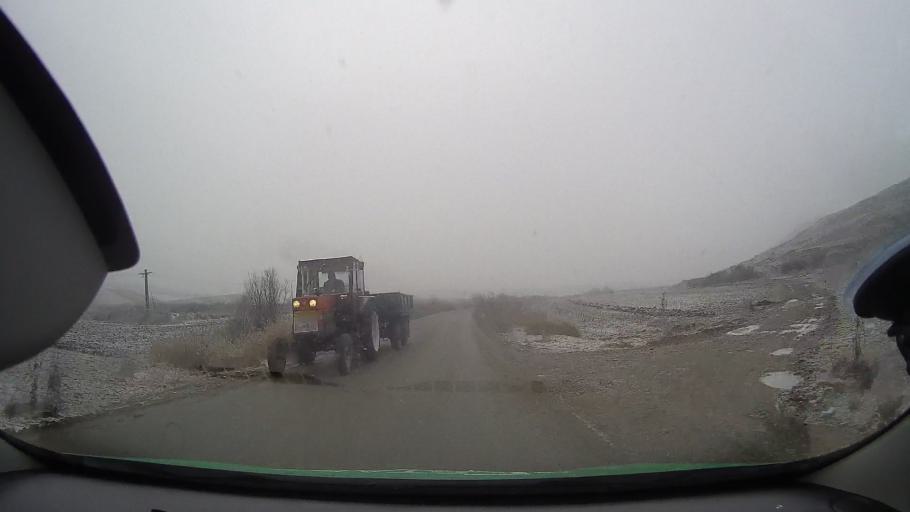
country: RO
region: Alba
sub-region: Comuna Noslac
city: Noslac
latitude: 46.3731
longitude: 23.9186
